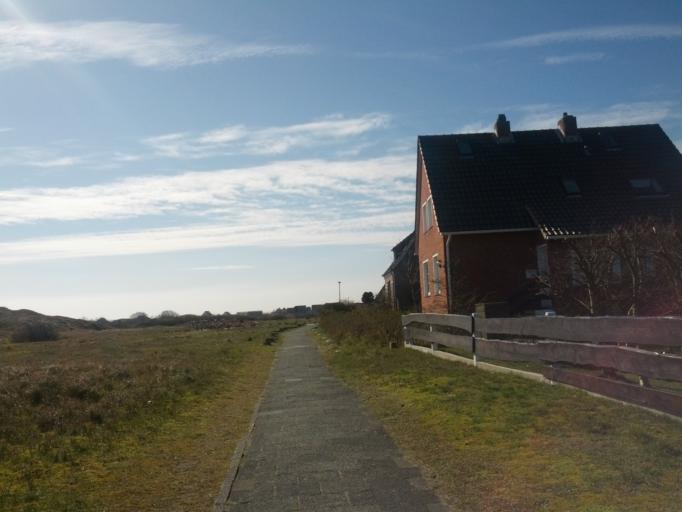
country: DE
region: Lower Saxony
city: Langeoog
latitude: 53.7519
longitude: 7.4909
